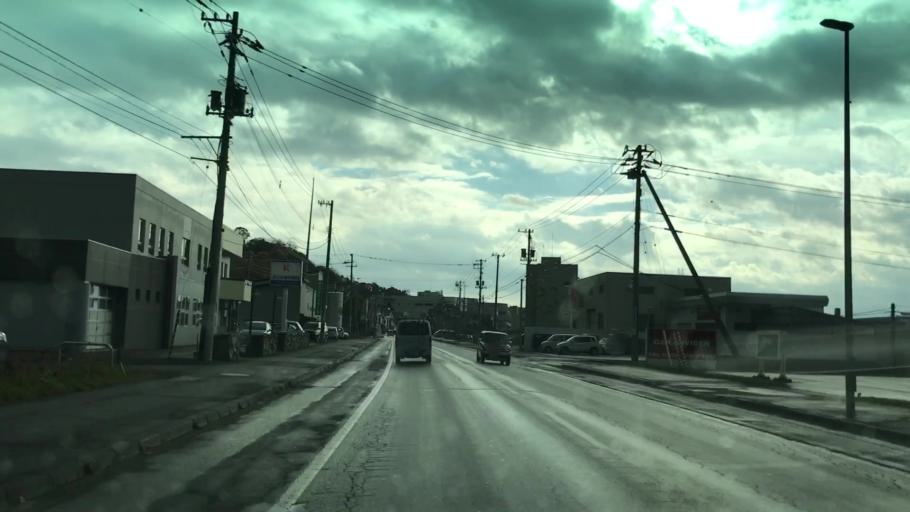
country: JP
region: Hokkaido
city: Shizunai-furukawacho
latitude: 42.1678
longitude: 142.7701
